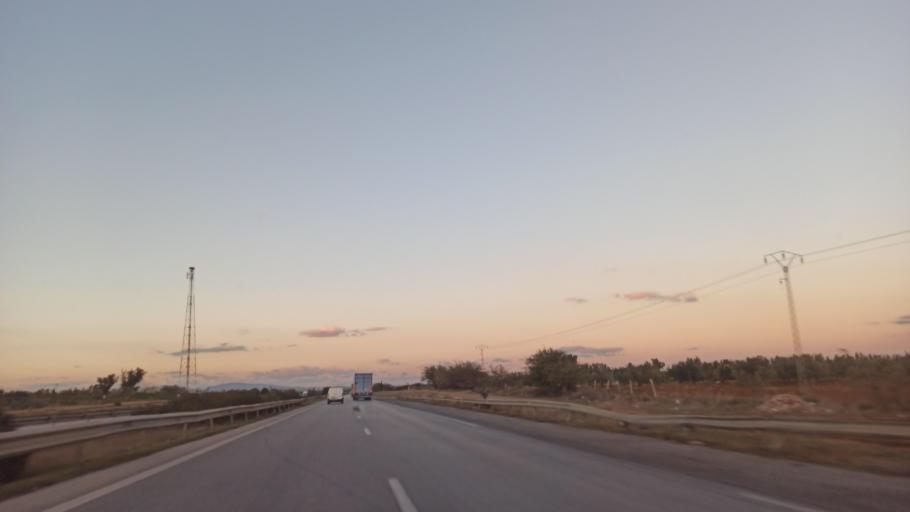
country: TN
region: Nabul
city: Al Hammamat
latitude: 36.2656
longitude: 10.4306
